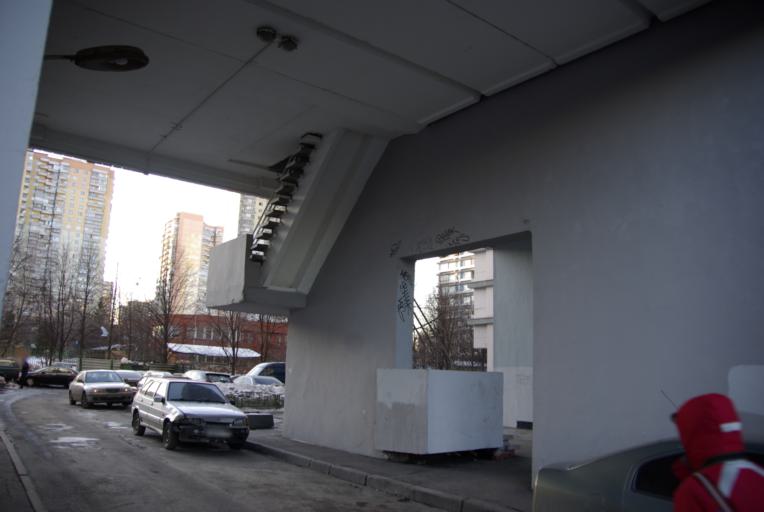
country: RU
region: Moscow
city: Nagornyy
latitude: 55.6389
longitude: 37.6004
